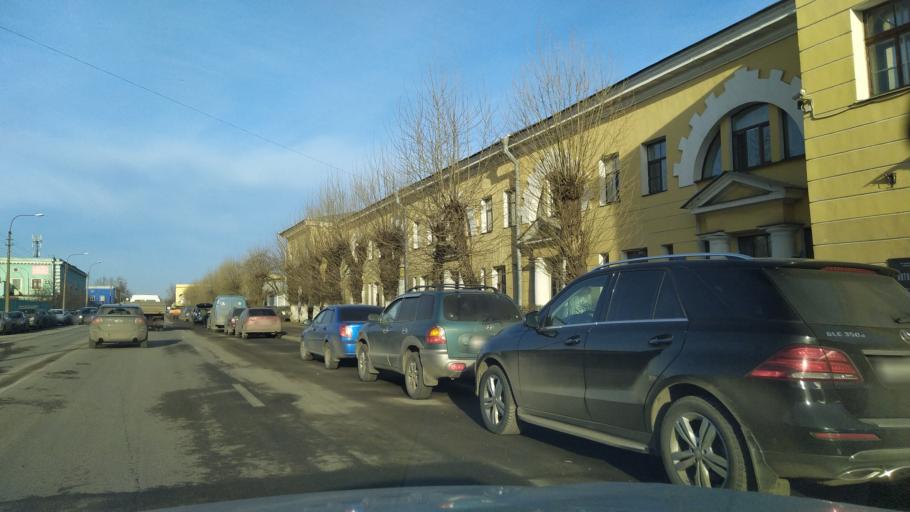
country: RU
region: St.-Petersburg
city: Kupchino
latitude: 59.8839
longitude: 30.3398
